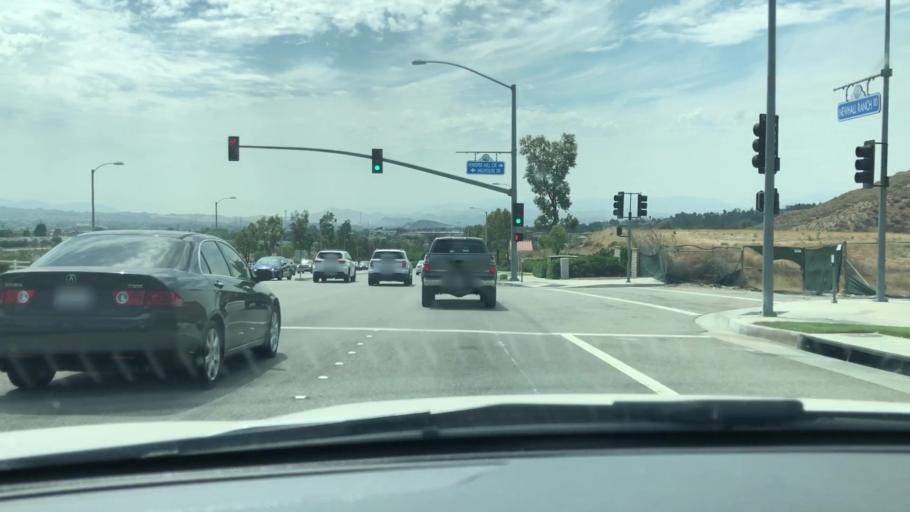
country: US
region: California
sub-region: Los Angeles County
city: Santa Clarita
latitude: 34.4251
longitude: -118.5289
